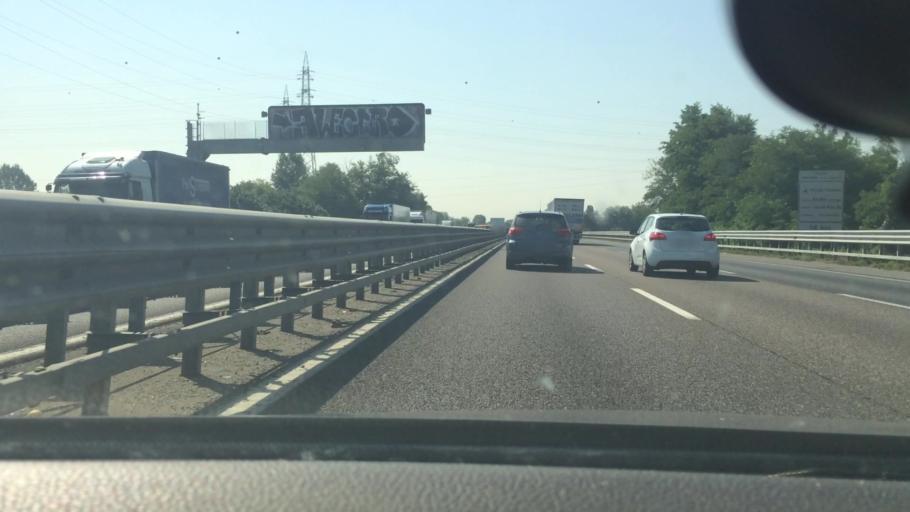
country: IT
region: Lombardy
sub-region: Citta metropolitana di Milano
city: Figino
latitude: 45.4788
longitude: 9.0752
